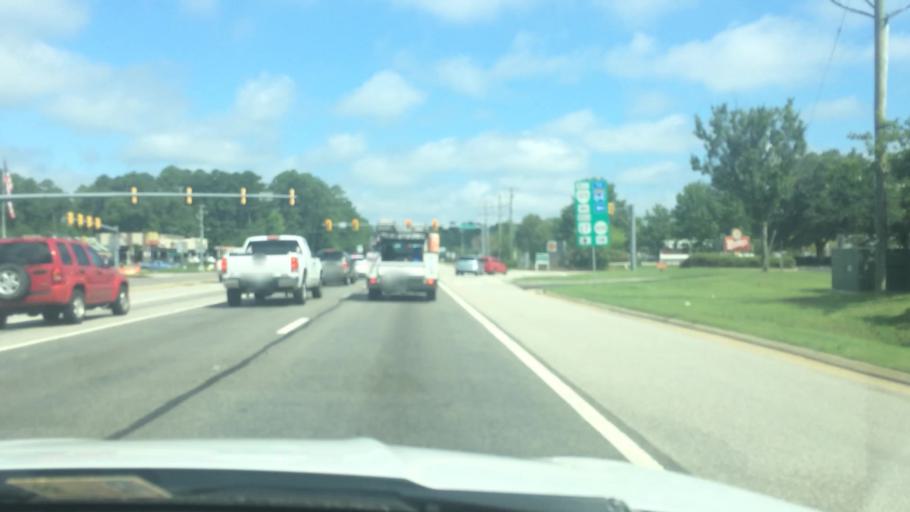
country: US
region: Virginia
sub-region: York County
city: Yorktown
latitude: 37.1892
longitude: -76.4870
